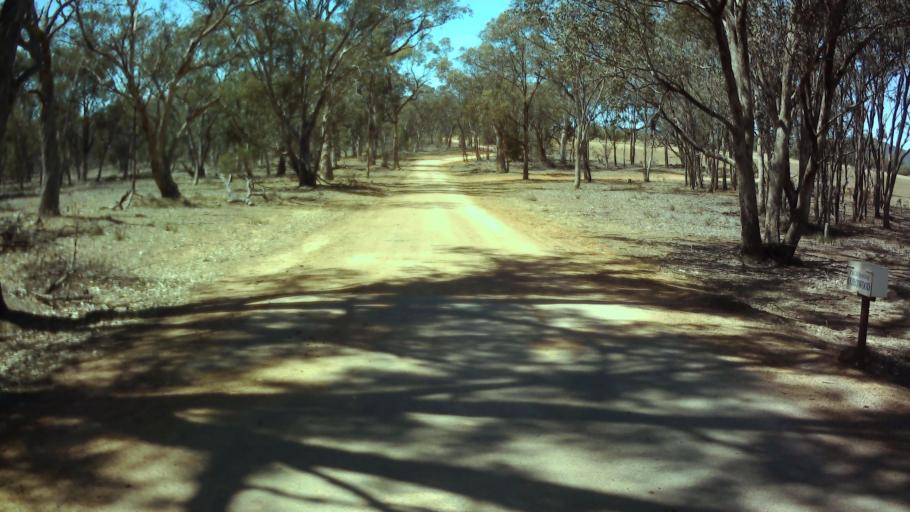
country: AU
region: New South Wales
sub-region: Weddin
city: Grenfell
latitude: -33.9408
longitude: 148.0782
